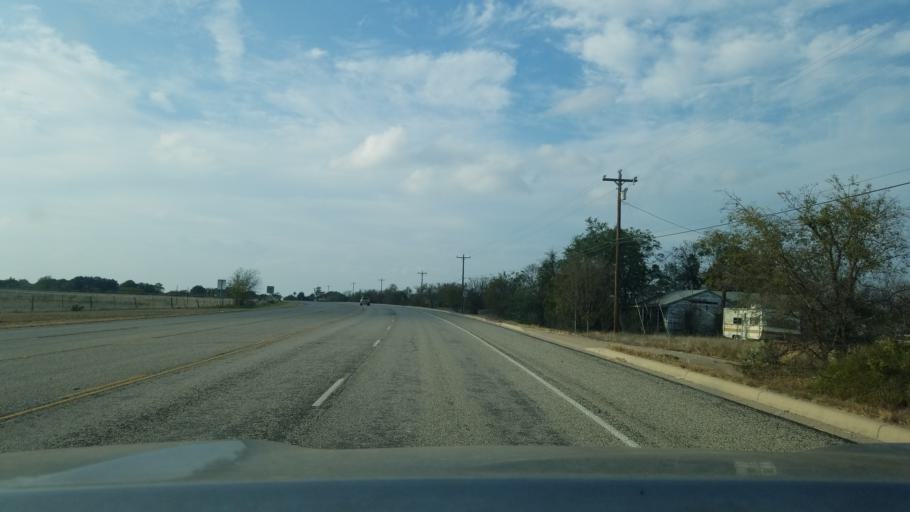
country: US
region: Texas
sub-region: Lampasas County
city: Lampasas
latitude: 31.2214
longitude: -98.3969
